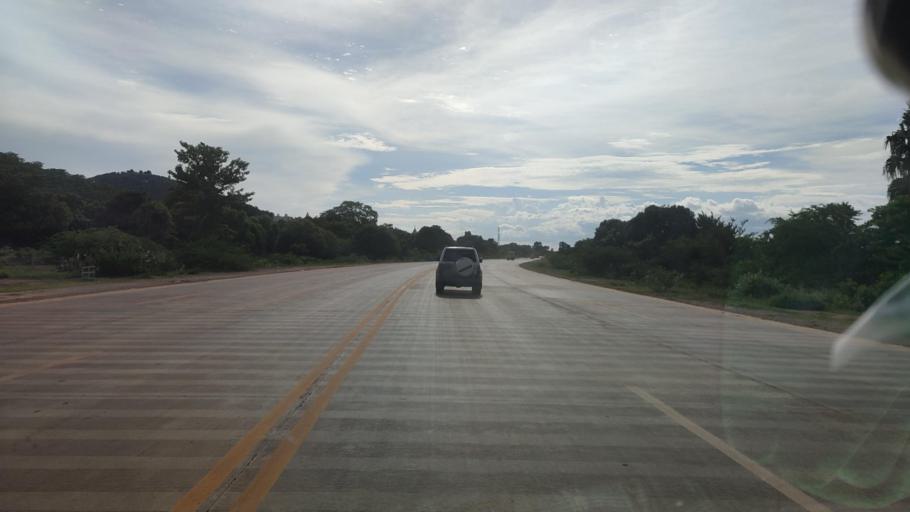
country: MM
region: Mandalay
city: Kyaukse
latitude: 21.6103
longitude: 96.1621
